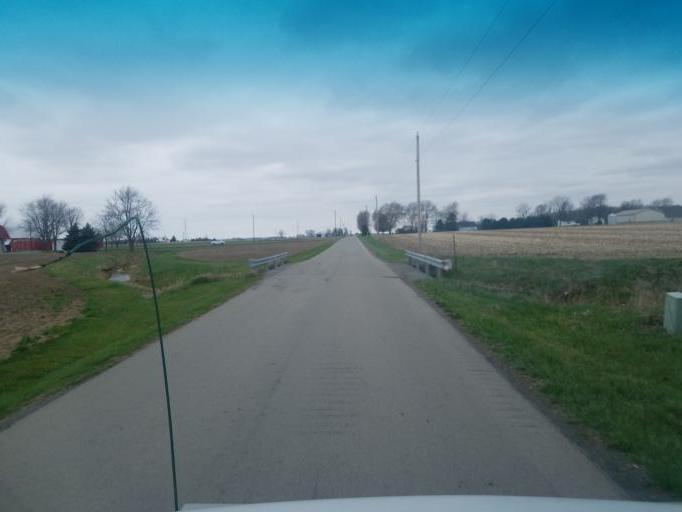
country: US
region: Ohio
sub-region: Allen County
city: Delphos
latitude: 40.9179
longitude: -84.3751
